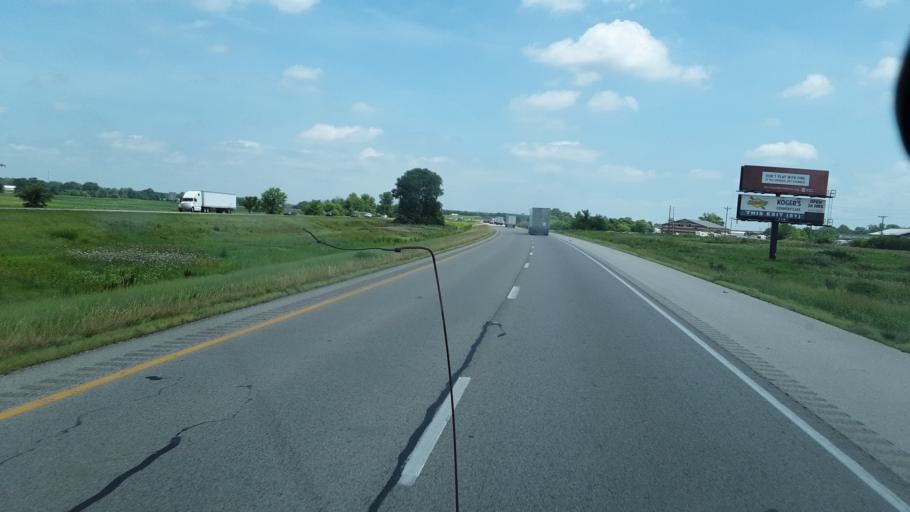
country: US
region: Indiana
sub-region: Putnam County
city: Cloverdale
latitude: 39.5632
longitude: -86.6429
